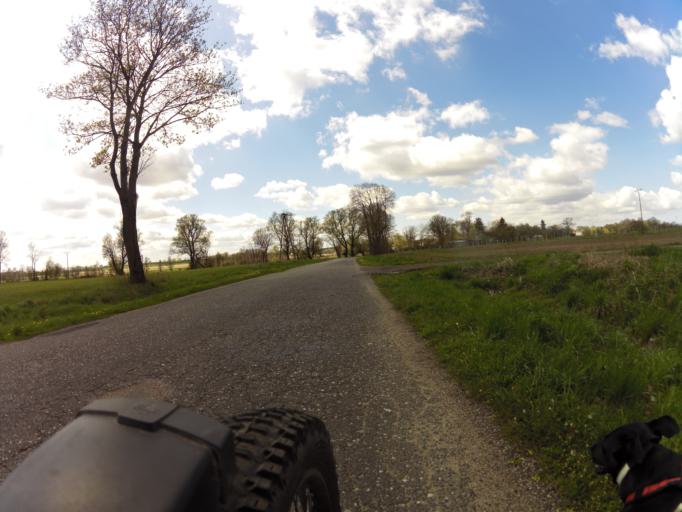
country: PL
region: West Pomeranian Voivodeship
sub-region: Powiat gryficki
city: Gryfice
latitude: 53.8597
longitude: 15.1762
